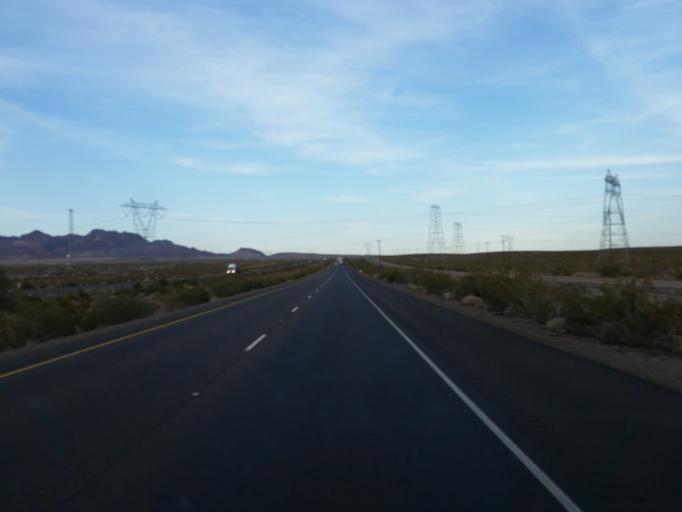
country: US
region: California
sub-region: San Bernardino County
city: Fort Irwin
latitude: 34.7784
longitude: -116.3941
